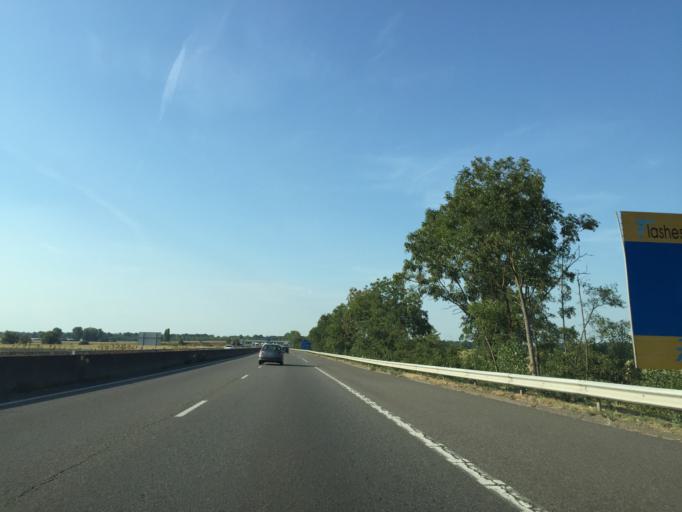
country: FR
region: Alsace
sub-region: Departement du Bas-Rhin
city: Reichstett
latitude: 48.6602
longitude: 7.7373
